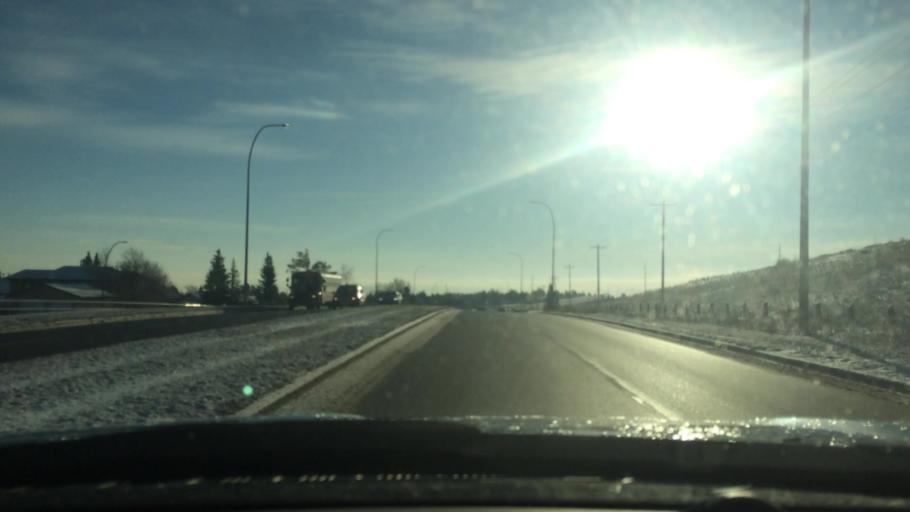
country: CA
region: Alberta
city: Calgary
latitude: 51.1275
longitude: -114.1029
